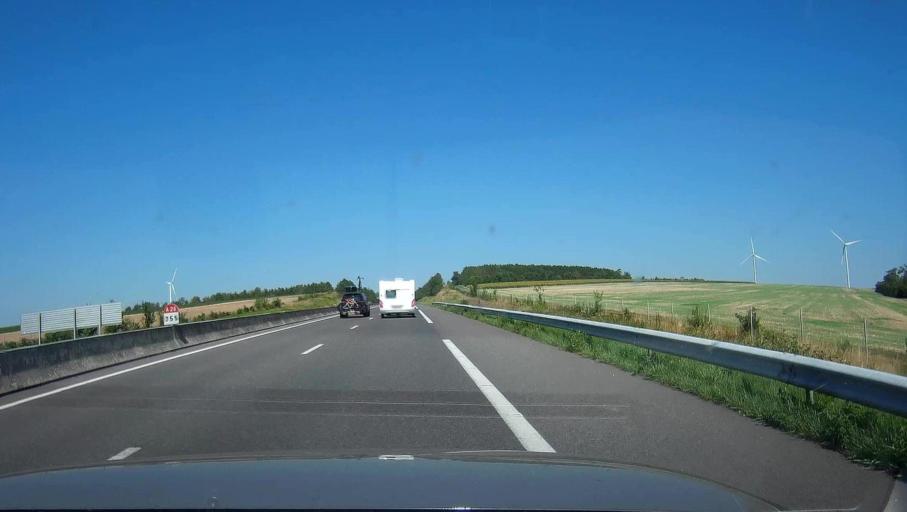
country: FR
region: Champagne-Ardenne
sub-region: Departement de l'Aube
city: Arcis-sur-Aube
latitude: 48.5729
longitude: 4.1908
